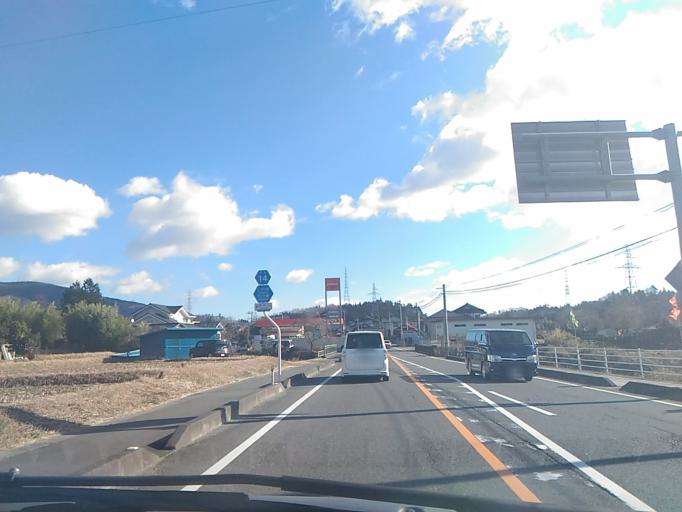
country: JP
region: Fukushima
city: Iwaki
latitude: 37.0071
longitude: 140.7508
